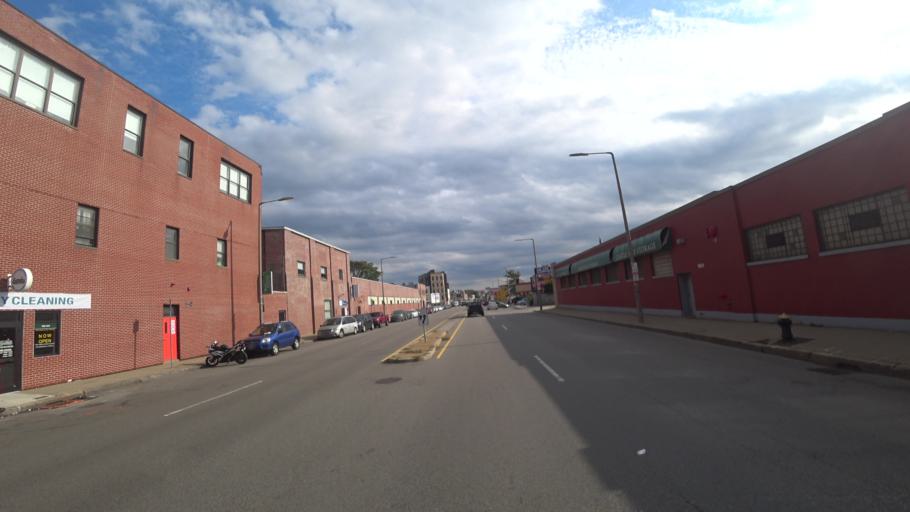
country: US
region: Massachusetts
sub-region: Suffolk County
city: South Boston
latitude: 42.3366
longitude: -71.0562
